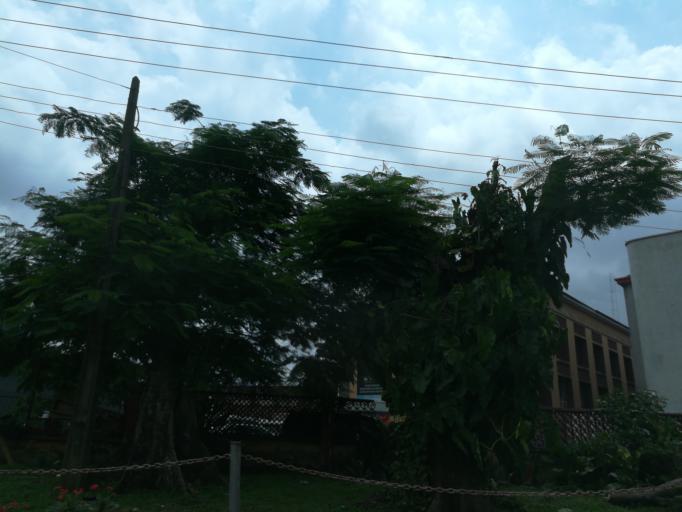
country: NG
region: Lagos
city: Ikeja
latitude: 6.5872
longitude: 3.3463
